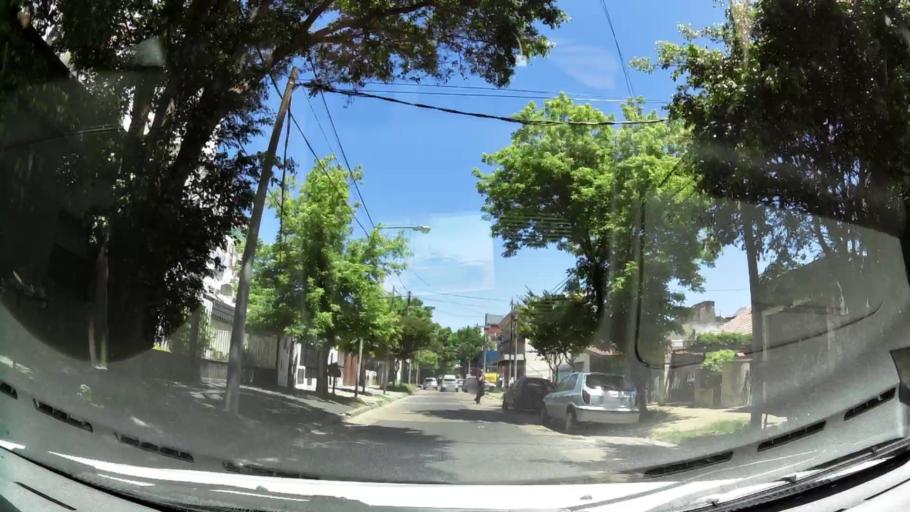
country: AR
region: Buenos Aires
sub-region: Partido de General San Martin
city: General San Martin
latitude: -34.5825
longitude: -58.5389
